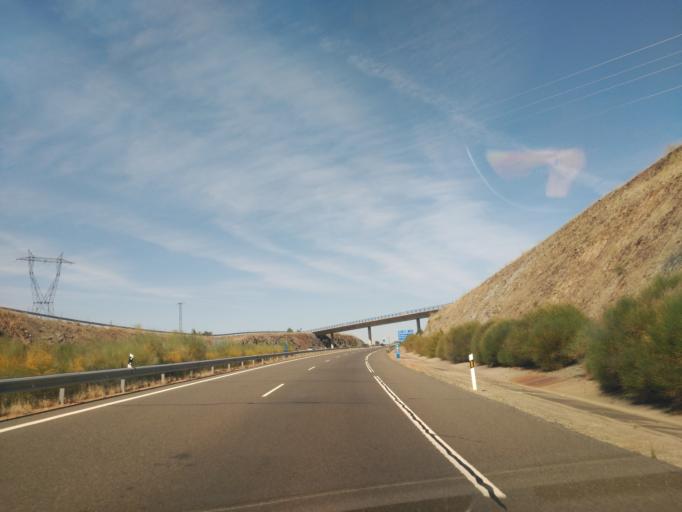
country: ES
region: Castille and Leon
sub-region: Provincia de Salamanca
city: Miranda de Azan
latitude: 40.8844
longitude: -5.6656
